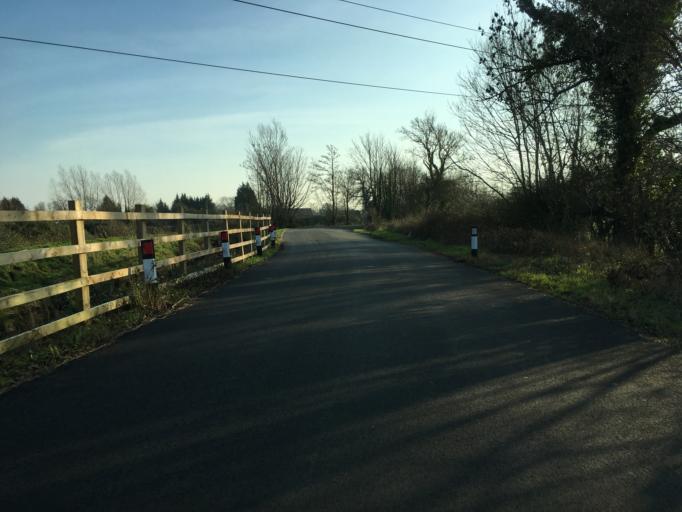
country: GB
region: Wales
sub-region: Newport
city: Goldcliff
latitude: 51.5626
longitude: -2.9104
